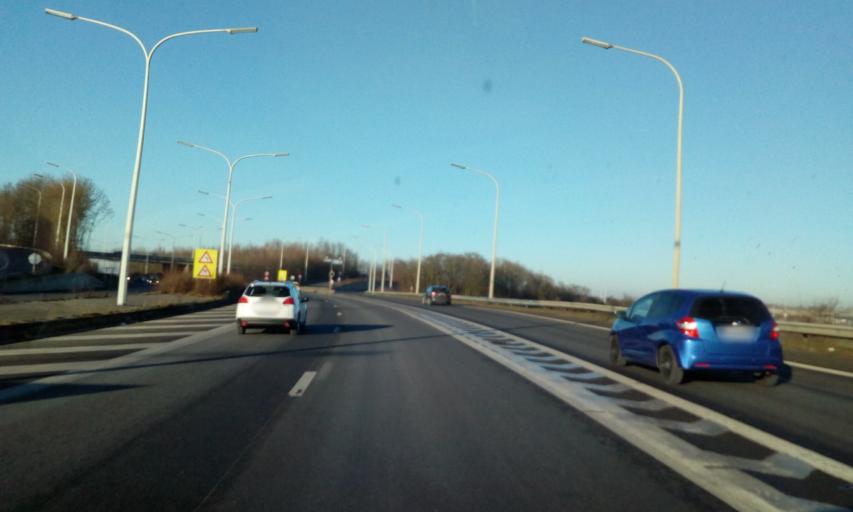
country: BE
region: Wallonia
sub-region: Province du Hainaut
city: Charleroi
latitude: 50.4503
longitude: 4.4424
